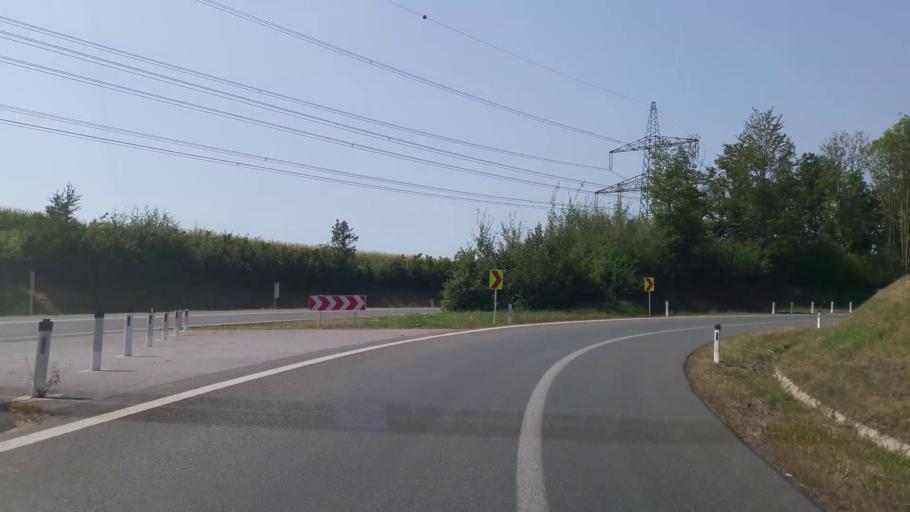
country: AT
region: Styria
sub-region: Politischer Bezirk Hartberg-Fuerstenfeld
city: Sankt Johann in der Haide
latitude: 47.2727
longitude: 16.0095
